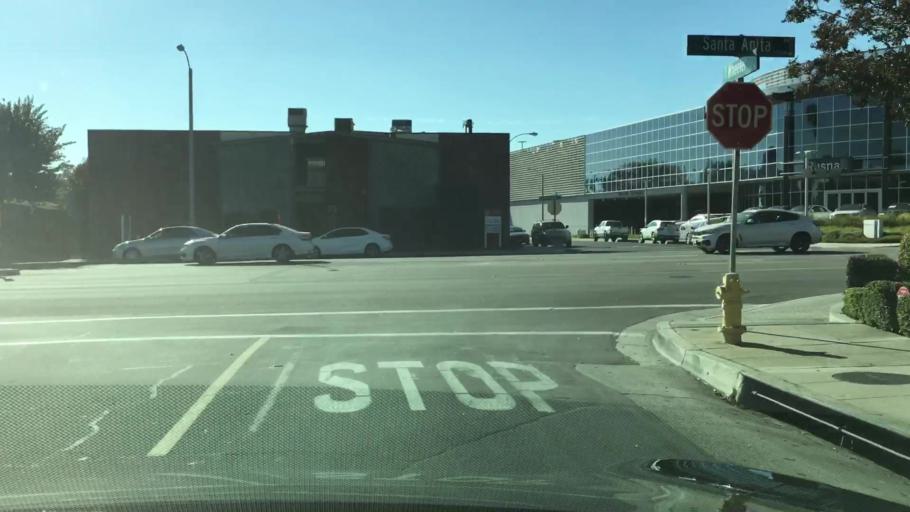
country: US
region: California
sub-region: Los Angeles County
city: Arcadia
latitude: 34.1413
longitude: -118.0312
